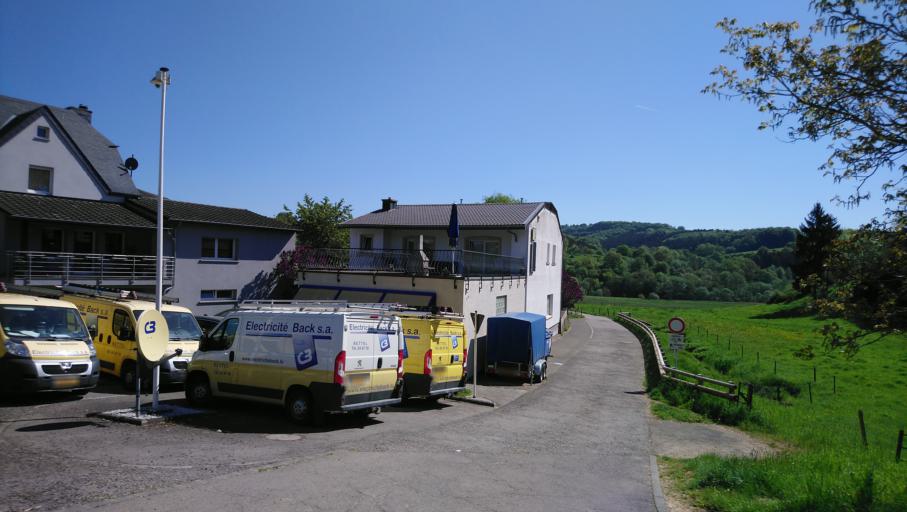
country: DE
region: Rheinland-Pfalz
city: Gentingen
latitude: 49.9181
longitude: 6.2258
